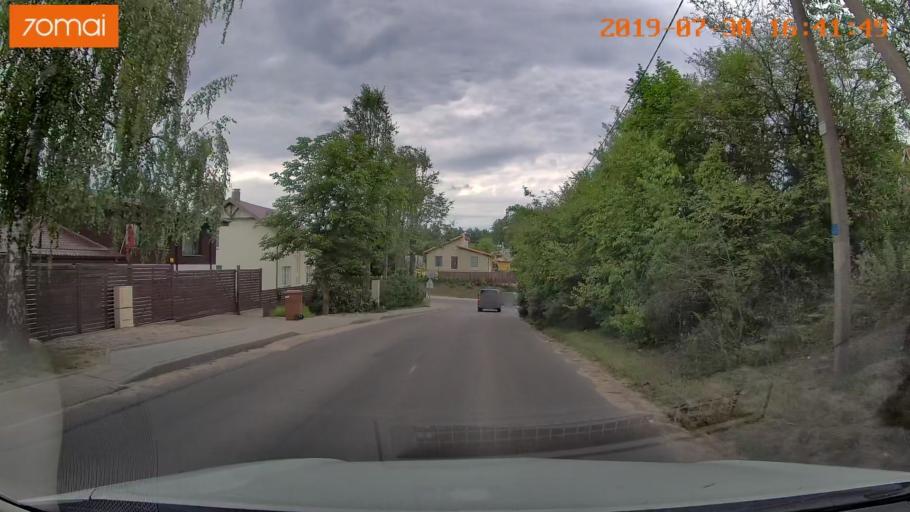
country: LT
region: Vilnius County
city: Rasos
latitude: 54.7139
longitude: 25.3517
